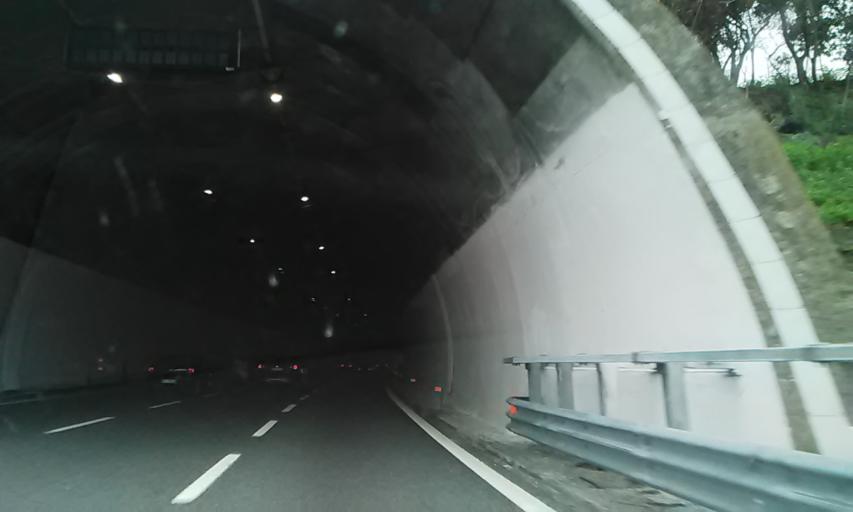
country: IT
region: Liguria
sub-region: Provincia di Genova
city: Cogoleto
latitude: 44.3944
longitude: 8.6500
